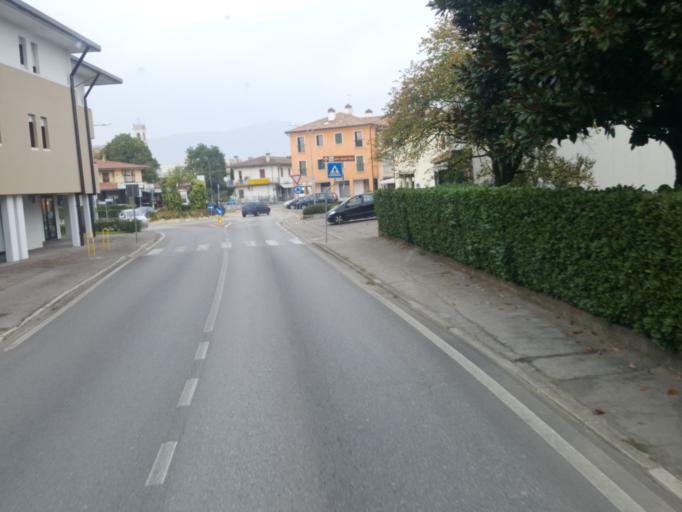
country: IT
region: Veneto
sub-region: Provincia di Treviso
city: Loria Bessica
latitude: 45.7264
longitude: 11.8658
